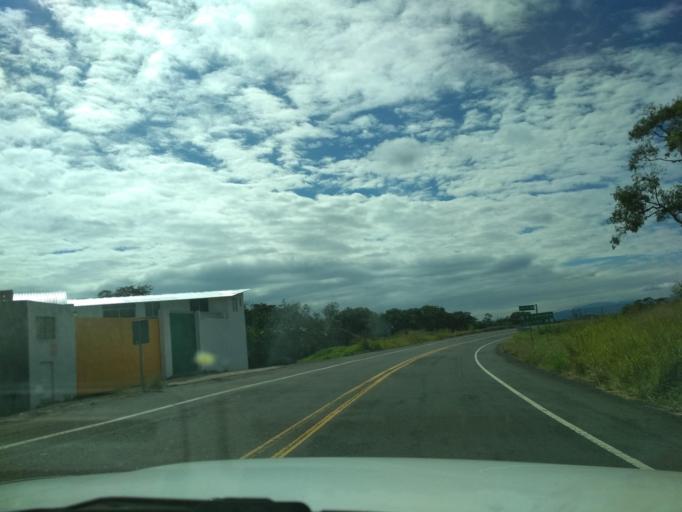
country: MX
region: Veracruz
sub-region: Coatepec
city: Las Lomas
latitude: 19.4500
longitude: -96.9273
